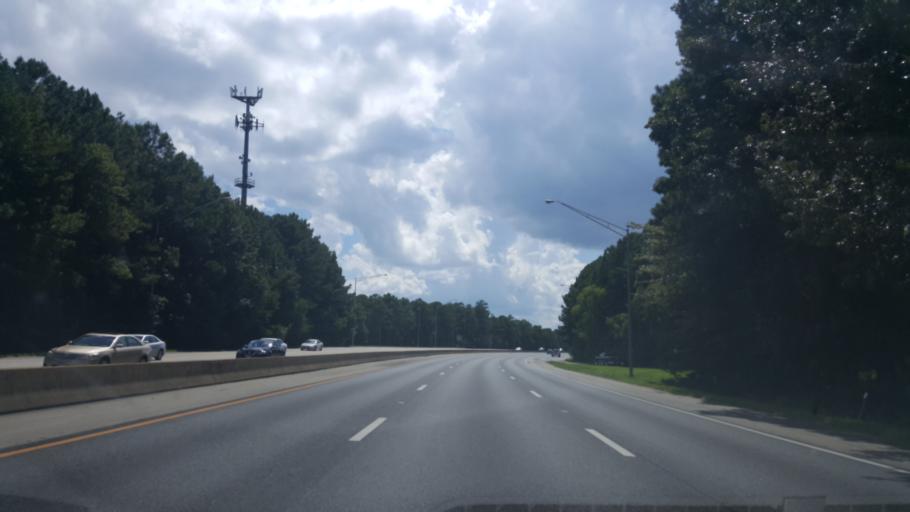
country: US
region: Virginia
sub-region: City of Hampton
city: Hampton
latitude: 37.0158
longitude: -76.3869
